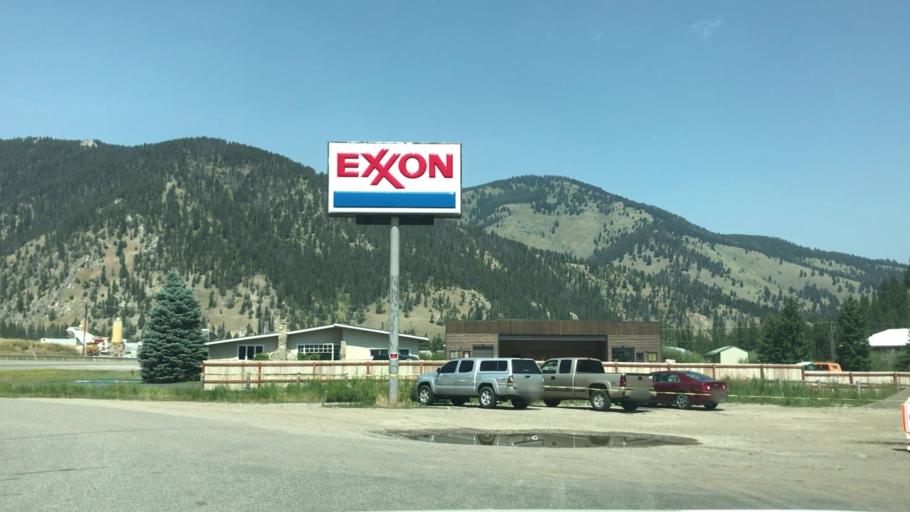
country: US
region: Montana
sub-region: Gallatin County
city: Big Sky
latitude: 45.2596
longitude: -111.2537
